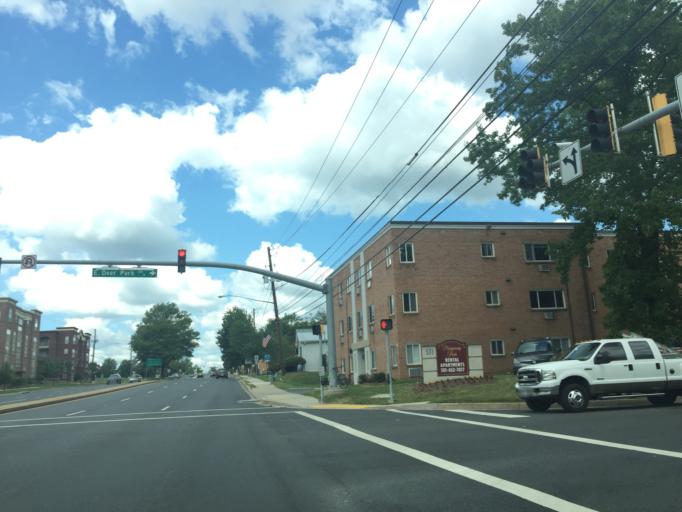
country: US
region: Maryland
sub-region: Montgomery County
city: Gaithersburg
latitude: 39.1321
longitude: -77.1887
